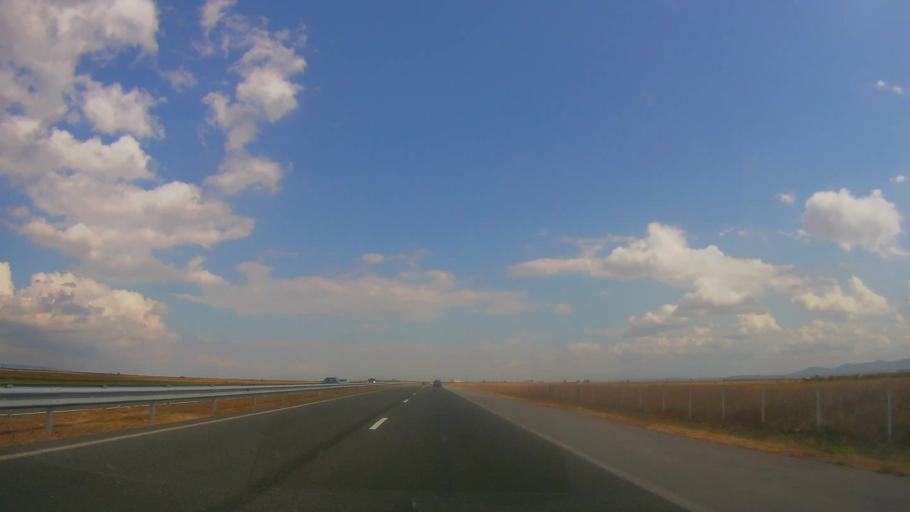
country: BG
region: Yambol
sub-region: Obshtina Yambol
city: Yambol
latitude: 42.5555
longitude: 26.5555
